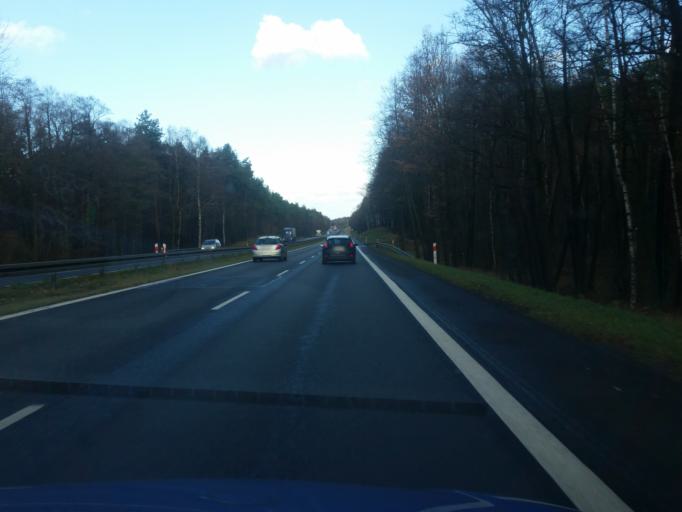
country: PL
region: Silesian Voivodeship
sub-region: Powiat czestochowski
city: Kamienica Polska
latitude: 50.6494
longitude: 19.1334
